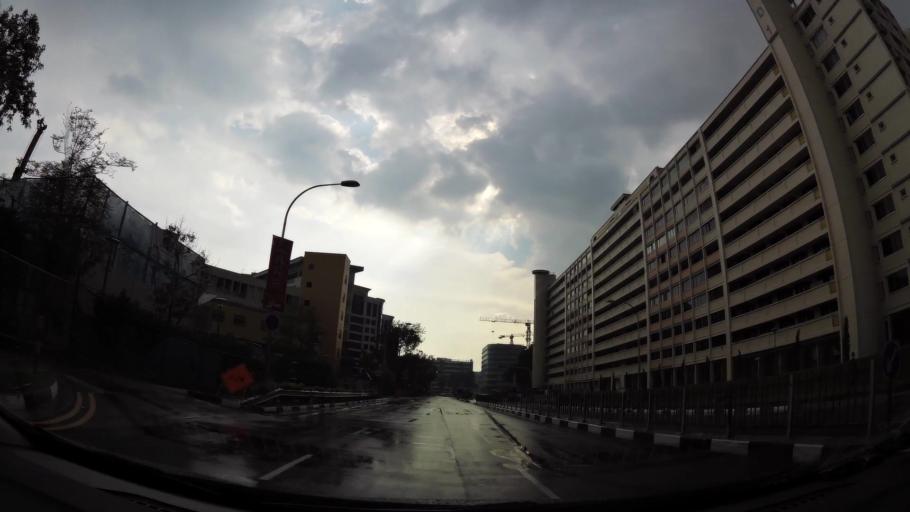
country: SG
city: Singapore
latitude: 1.3410
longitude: 103.9522
